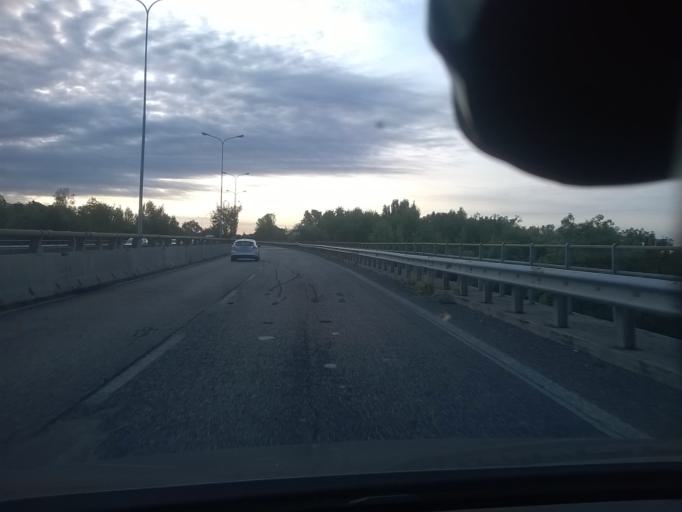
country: IT
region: Lombardy
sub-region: Provincia di Bergamo
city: Grassobbio
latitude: 45.6691
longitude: 9.7273
